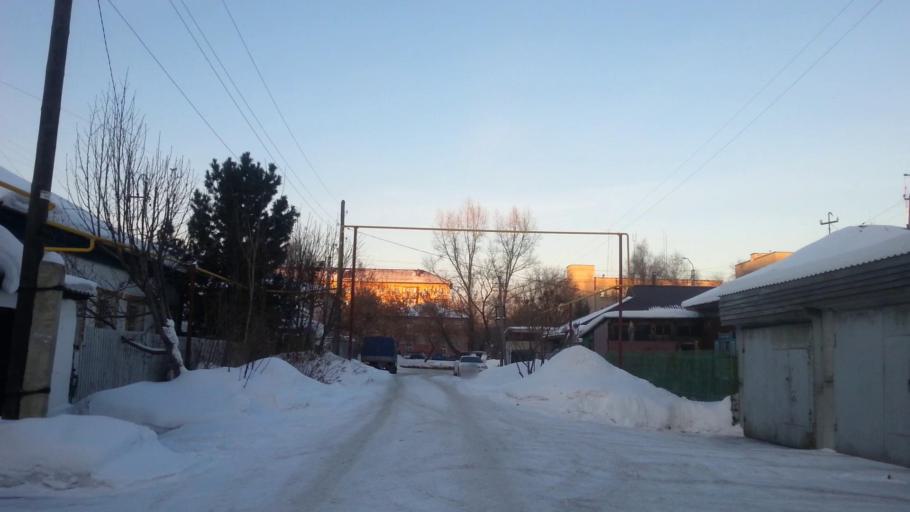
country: RU
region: Altai Krai
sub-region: Gorod Barnaulskiy
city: Barnaul
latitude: 53.3557
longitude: 83.7024
